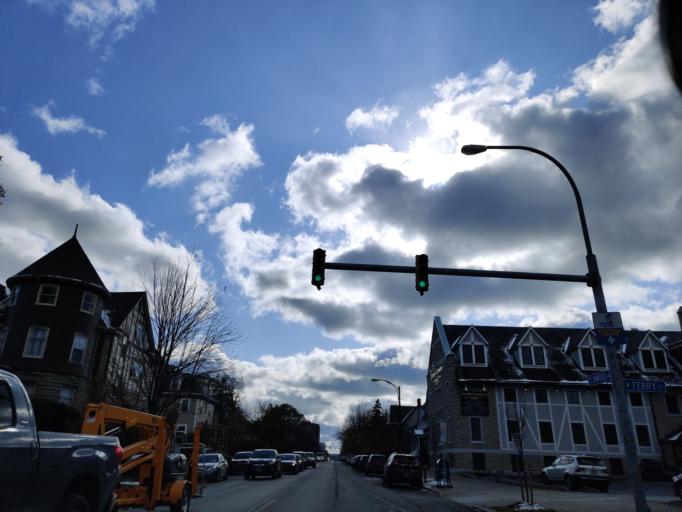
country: US
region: New York
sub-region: Erie County
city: Buffalo
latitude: 42.9155
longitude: -78.8771
